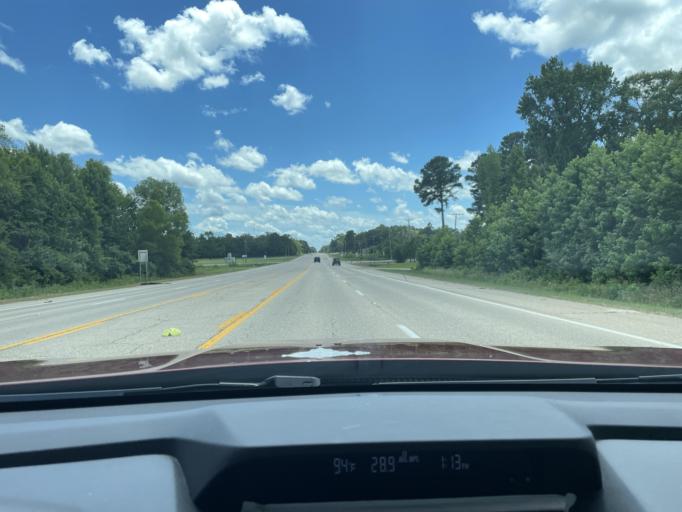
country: US
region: Arkansas
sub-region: Drew County
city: Monticello
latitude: 33.6711
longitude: -91.8043
